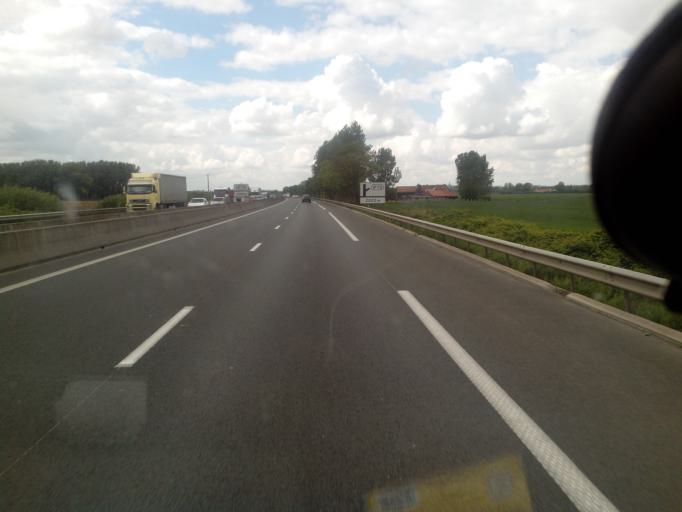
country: FR
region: Nord-Pas-de-Calais
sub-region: Departement du Nord
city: Steenwerck
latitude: 50.7109
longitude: 2.7764
